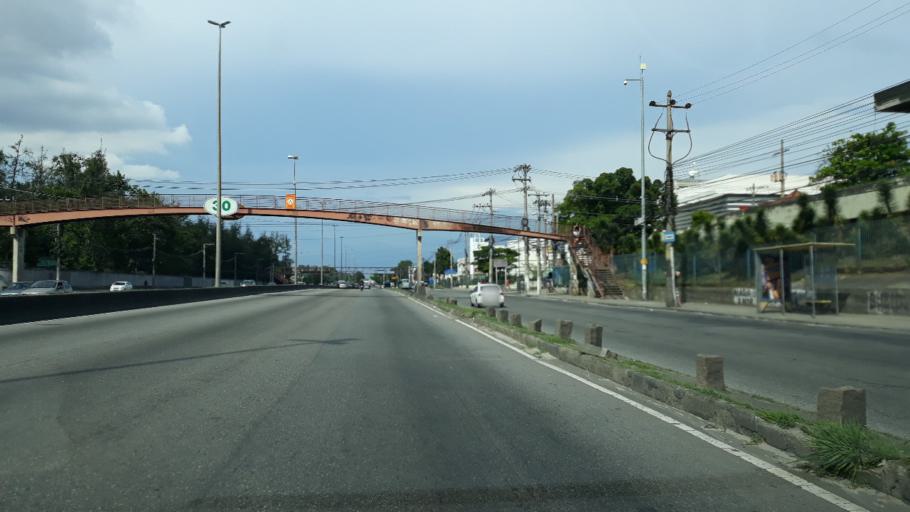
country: BR
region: Rio de Janeiro
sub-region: Sao Joao De Meriti
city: Sao Joao de Meriti
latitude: -22.8417
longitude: -43.3716
